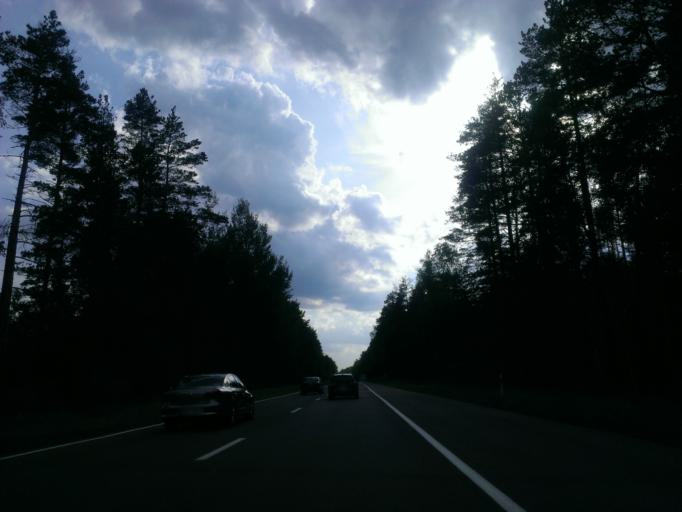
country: LV
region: Incukalns
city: Vangazi
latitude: 57.1049
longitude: 24.5961
